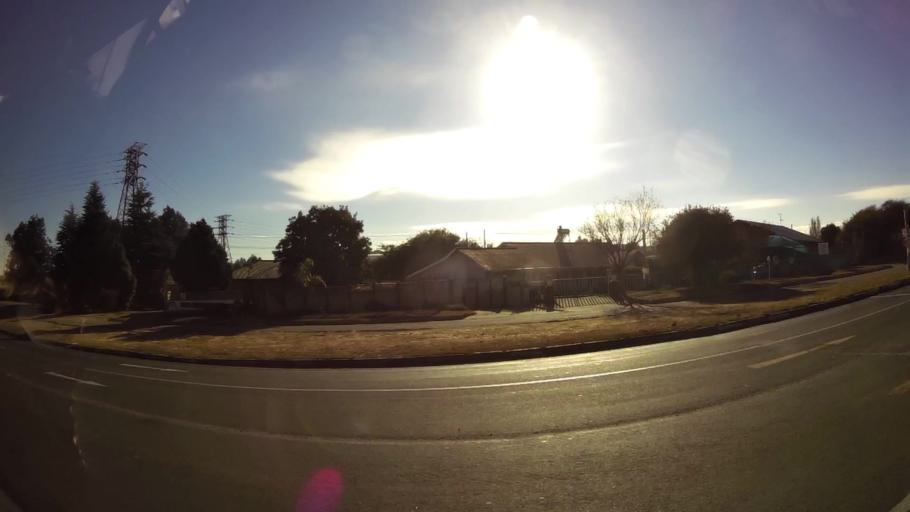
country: ZA
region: Gauteng
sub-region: West Rand District Municipality
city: Krugersdorp
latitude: -26.1190
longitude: 27.8022
